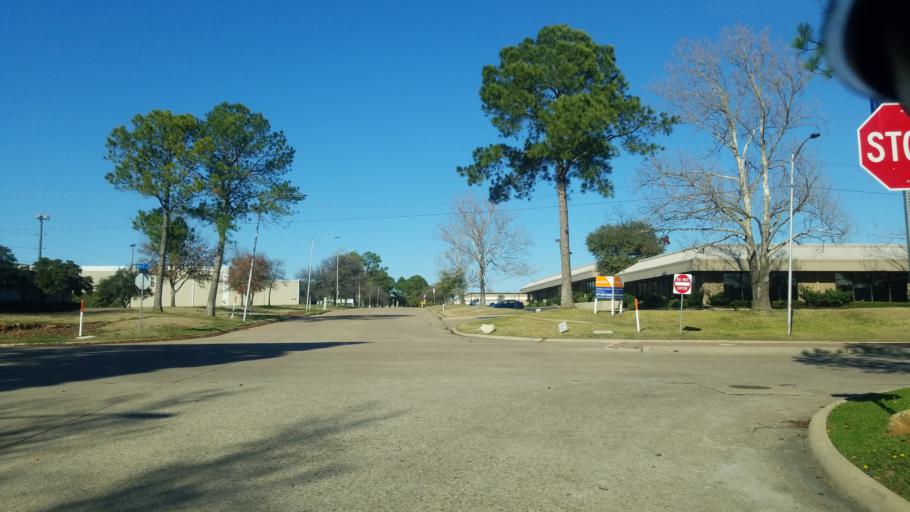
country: US
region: Texas
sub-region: Tarrant County
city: Arlington
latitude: 32.7671
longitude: -97.0679
